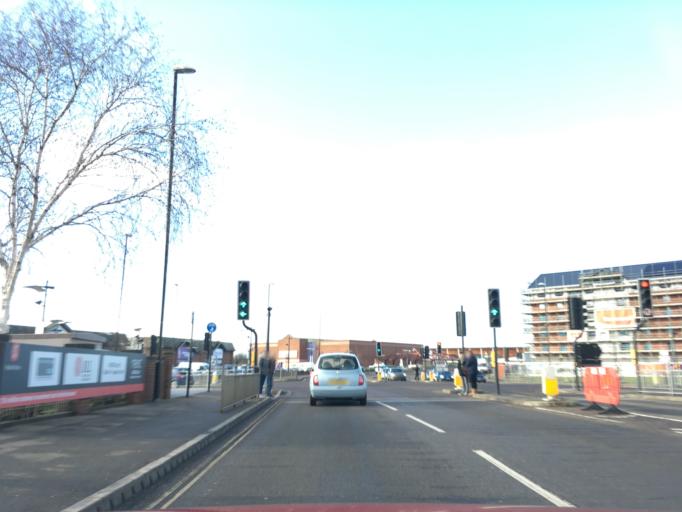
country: GB
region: England
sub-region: Gloucestershire
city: Gloucester
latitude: 51.8585
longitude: -2.2522
